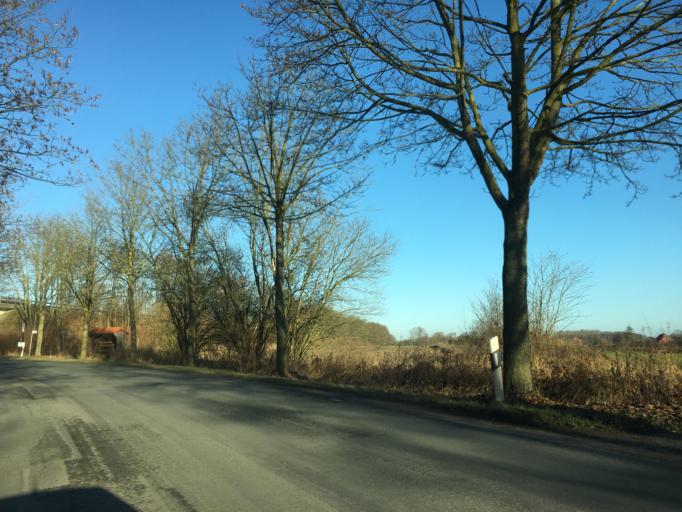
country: DE
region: North Rhine-Westphalia
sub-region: Regierungsbezirk Munster
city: Dulmen
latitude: 51.8531
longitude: 7.2915
